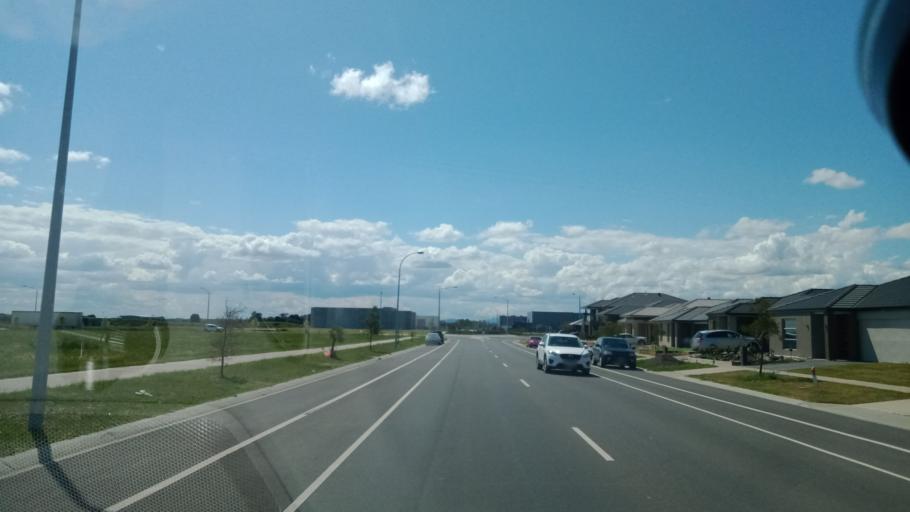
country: AU
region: Victoria
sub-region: Casey
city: Cranbourne West
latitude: -38.0953
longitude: 145.2502
